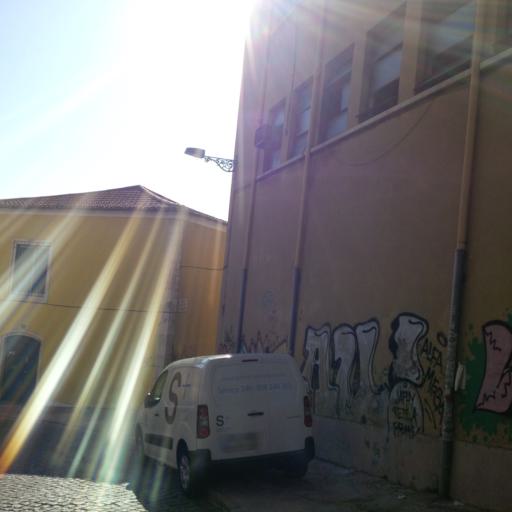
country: PT
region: Lisbon
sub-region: Lisbon
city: Lisbon
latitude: 38.7152
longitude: -9.1227
